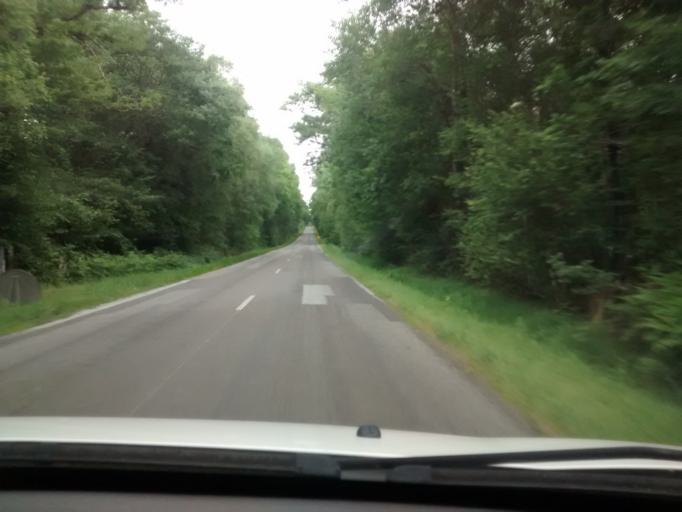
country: FR
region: Brittany
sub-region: Departement d'Ille-et-Vilaine
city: Servon-sur-Vilaine
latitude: 48.1476
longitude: -1.4459
